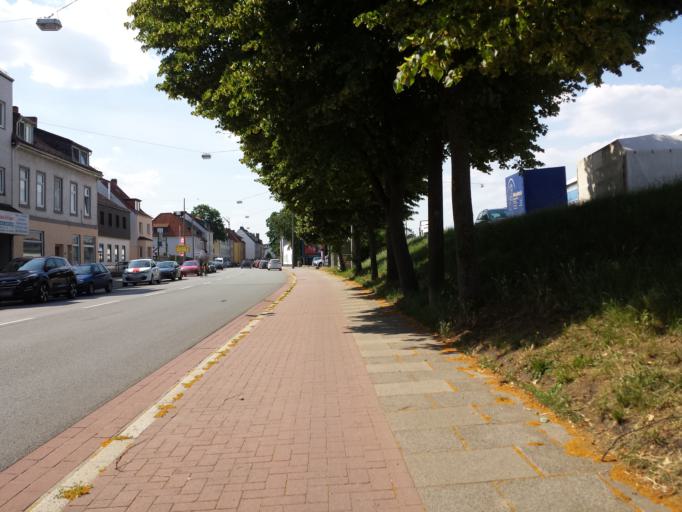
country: DE
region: Bremen
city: Bremen
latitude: 53.0787
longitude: 8.7792
